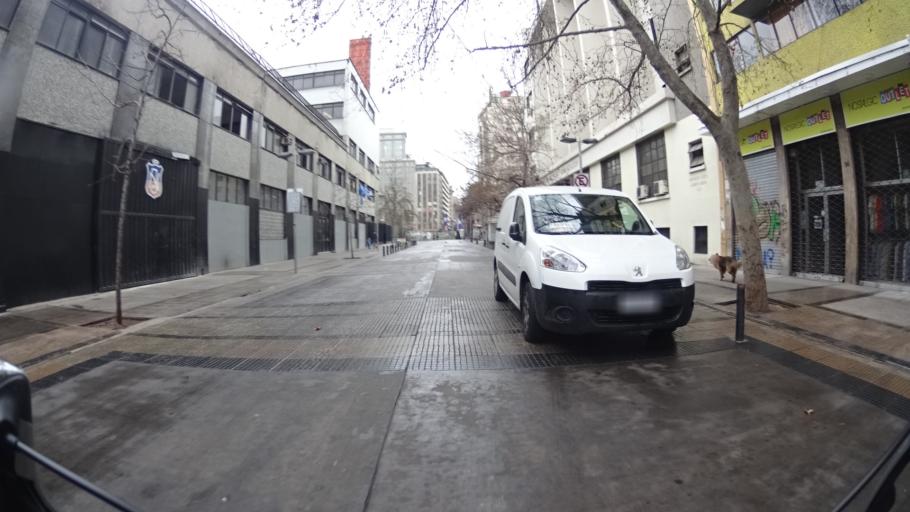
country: CL
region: Santiago Metropolitan
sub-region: Provincia de Santiago
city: Santiago
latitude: -33.4454
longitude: -70.6501
